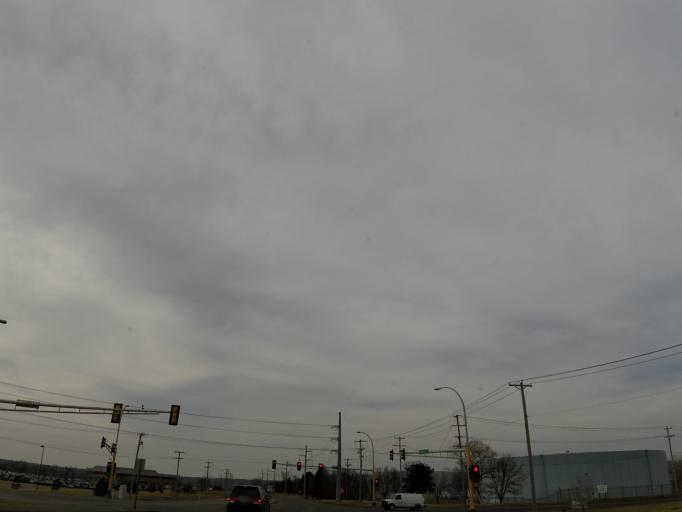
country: US
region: Minnesota
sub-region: Dakota County
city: Inver Grove Heights
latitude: 44.7791
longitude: -93.0377
